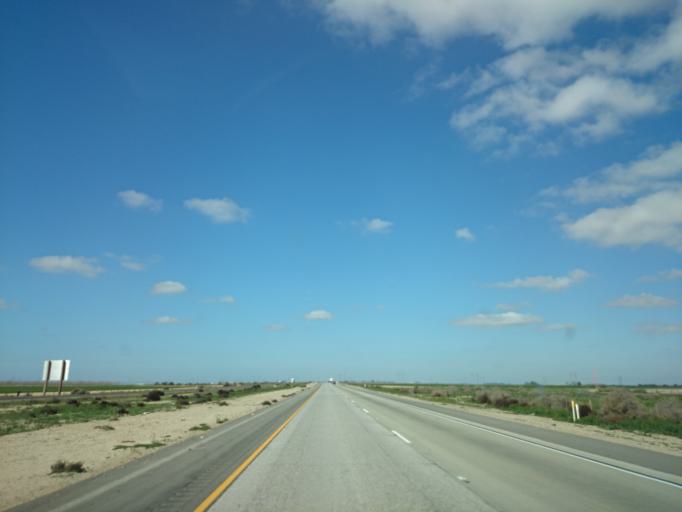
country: US
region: California
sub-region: Kern County
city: Buttonwillow
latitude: 35.3677
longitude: -119.3537
